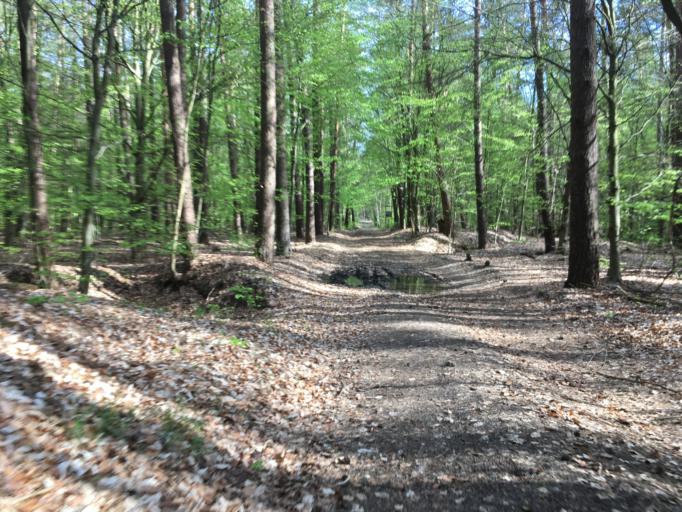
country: DE
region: Brandenburg
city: Bernau bei Berlin
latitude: 52.7180
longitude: 13.5637
